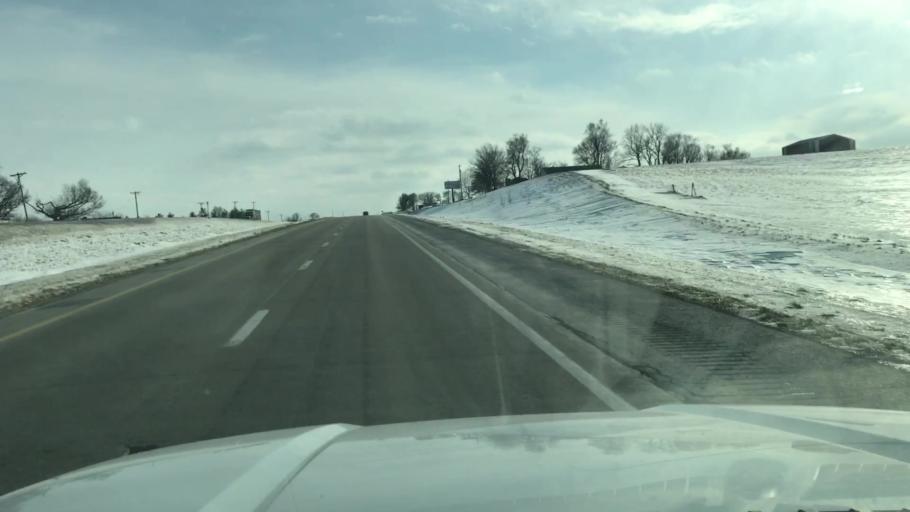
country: US
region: Missouri
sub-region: Nodaway County
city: Maryville
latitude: 40.2938
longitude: -94.8755
